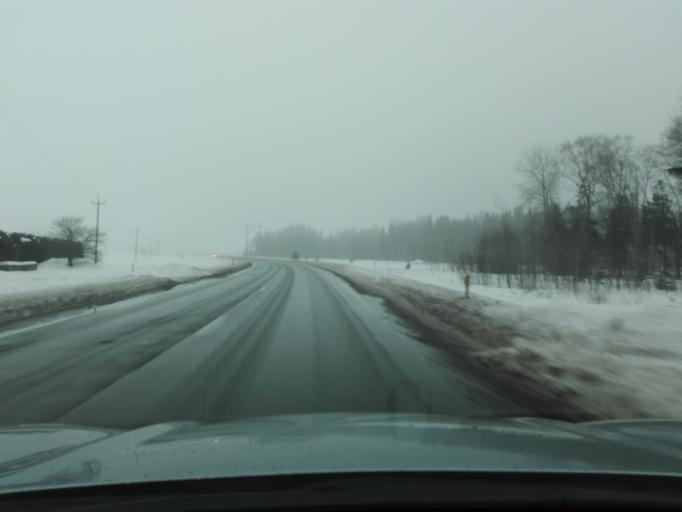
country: EE
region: Raplamaa
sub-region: Kohila vald
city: Kohila
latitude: 59.2170
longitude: 24.7761
